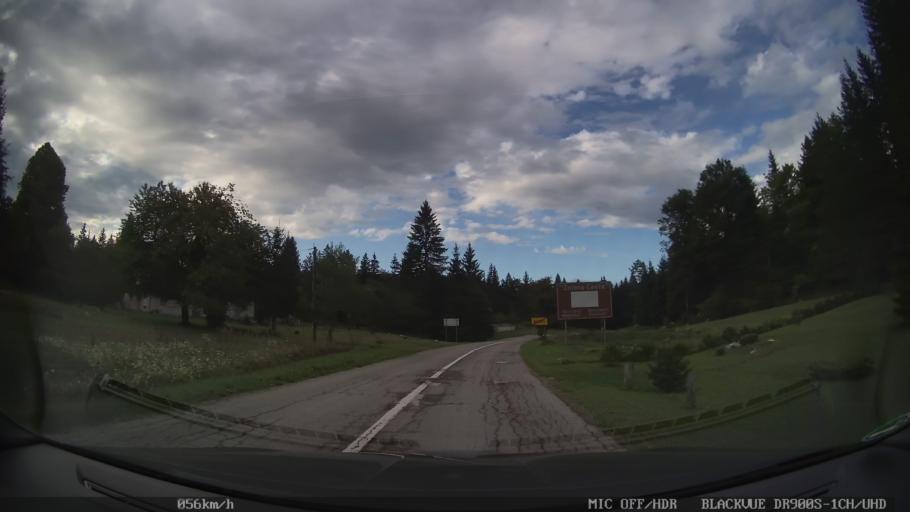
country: HR
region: Licko-Senjska
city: Jezerce
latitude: 44.9580
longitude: 15.5256
